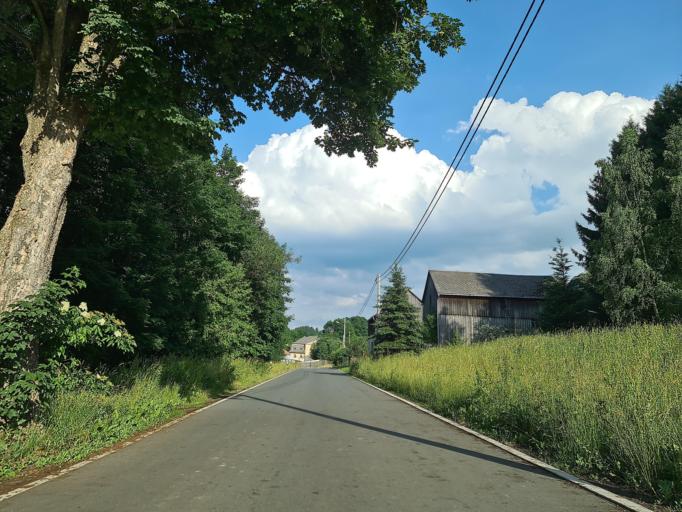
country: DE
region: Saxony
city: Bosenbrunn
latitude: 50.3987
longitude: 12.0968
